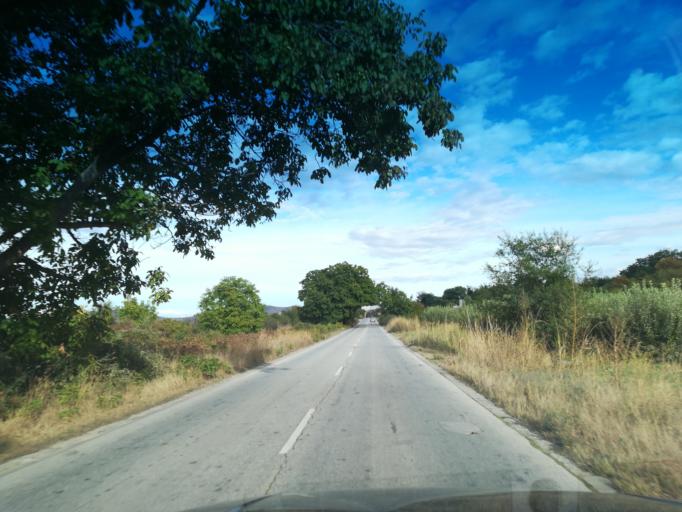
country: BG
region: Pazardzhik
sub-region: Obshtina Bratsigovo
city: Bratsigovo
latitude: 42.0690
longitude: 24.3960
